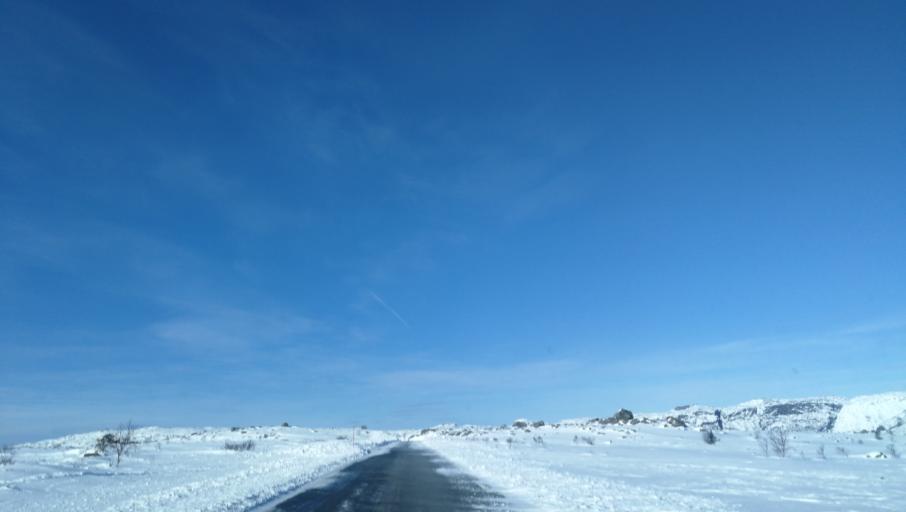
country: NO
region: Rogaland
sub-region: Hjelmeland
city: Hjelmelandsvagen
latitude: 59.1075
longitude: 6.3741
